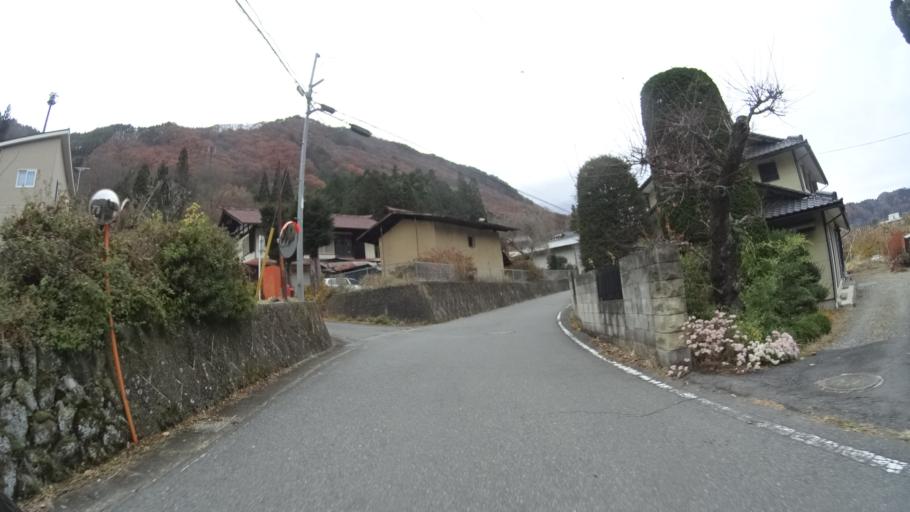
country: JP
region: Gunma
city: Numata
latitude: 36.6926
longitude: 139.2079
